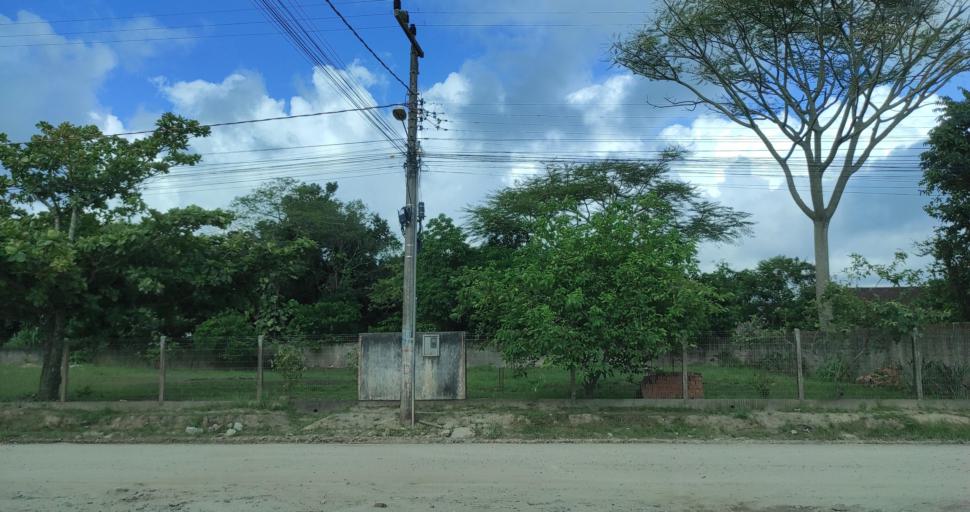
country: BR
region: Santa Catarina
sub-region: Porto Belo
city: Porto Belo
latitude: -27.1837
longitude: -48.5106
